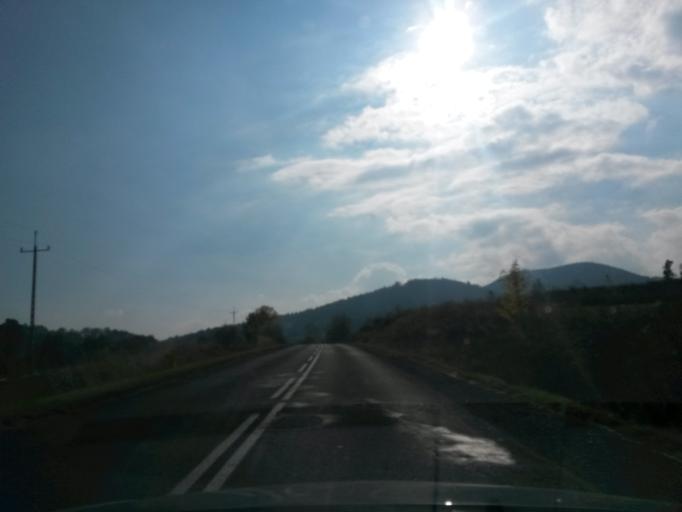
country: PL
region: Lower Silesian Voivodeship
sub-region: Powiat jeleniogorski
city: Sosnowka
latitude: 50.8239
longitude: 15.7265
